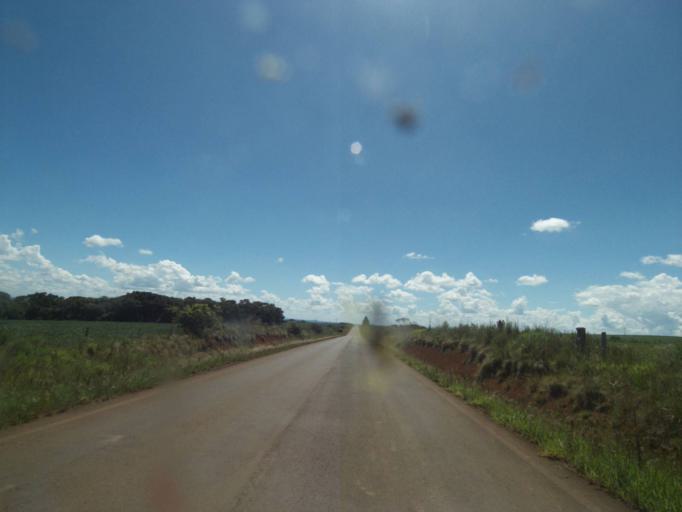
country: BR
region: Parana
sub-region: Pinhao
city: Pinhao
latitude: -25.8133
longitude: -52.0480
